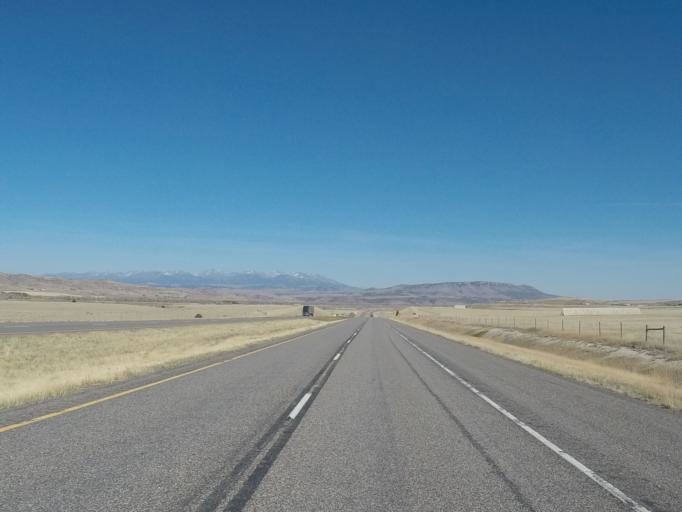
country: US
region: Montana
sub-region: Park County
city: Livingston
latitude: 45.6692
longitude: -110.5221
